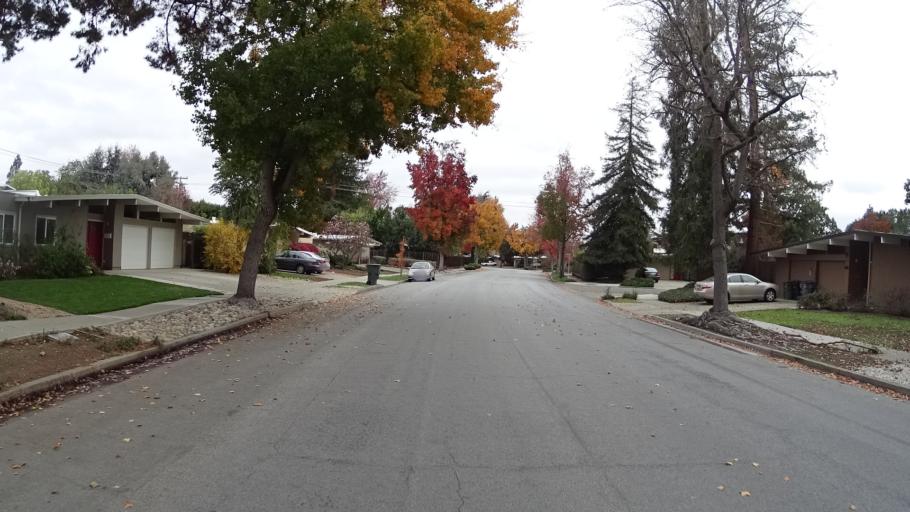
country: US
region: California
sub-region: Santa Clara County
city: Sunnyvale
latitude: 37.3556
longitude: -122.0488
